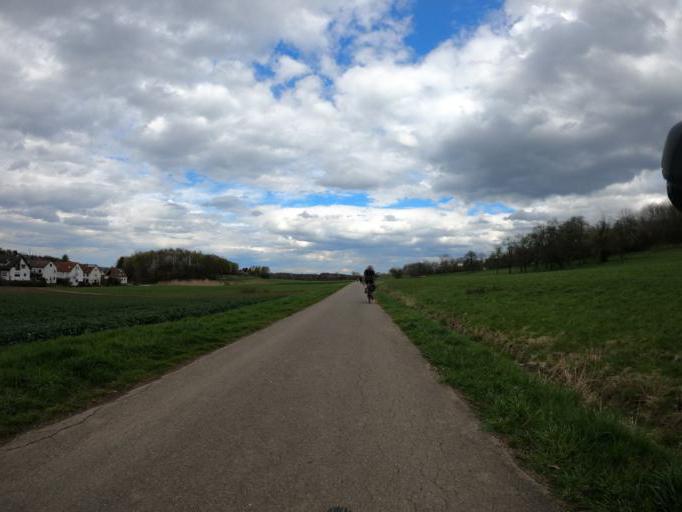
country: DE
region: Baden-Wuerttemberg
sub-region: Tuebingen Region
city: Wannweil
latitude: 48.4809
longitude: 9.1479
